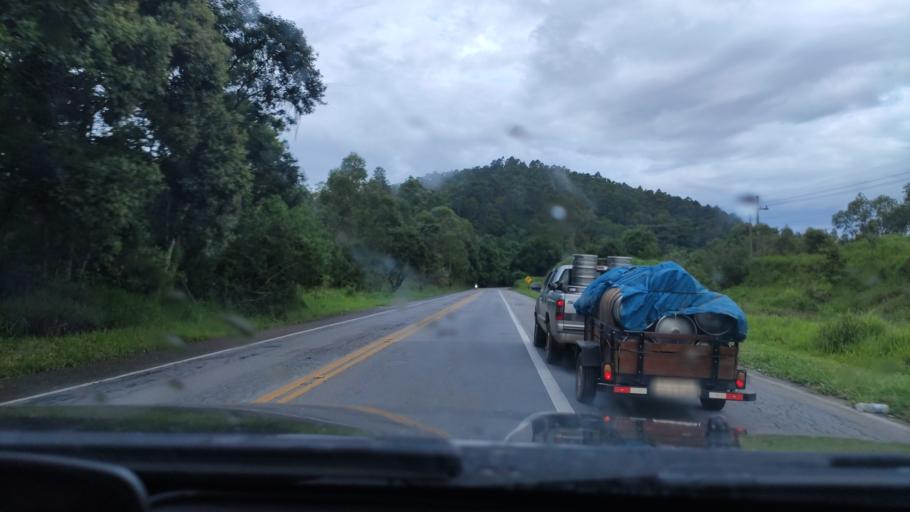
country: BR
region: Sao Paulo
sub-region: Braganca Paulista
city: Braganca Paulista
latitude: -22.8249
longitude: -46.5554
